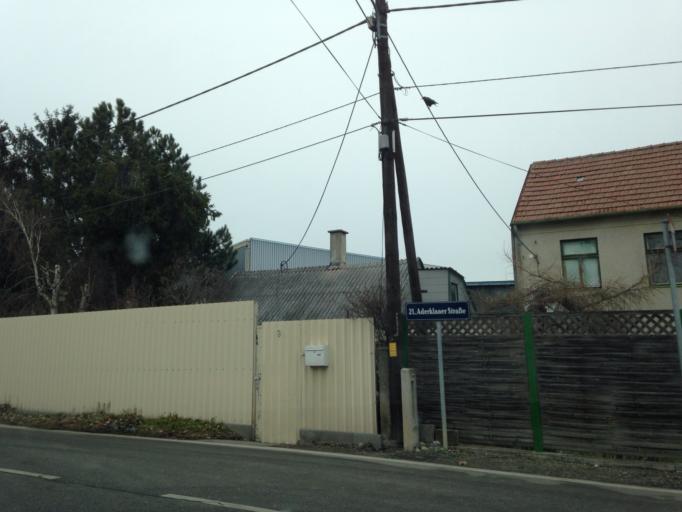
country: AT
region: Lower Austria
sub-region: Politischer Bezirk Wien-Umgebung
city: Gerasdorf bei Wien
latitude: 48.2621
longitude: 16.4487
